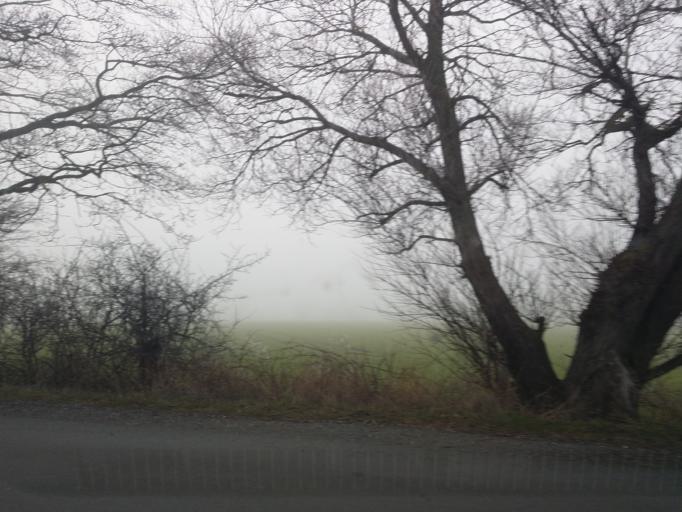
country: DE
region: Schleswig-Holstein
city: Burg auf Fehmarn
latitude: 54.4197
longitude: 11.2427
